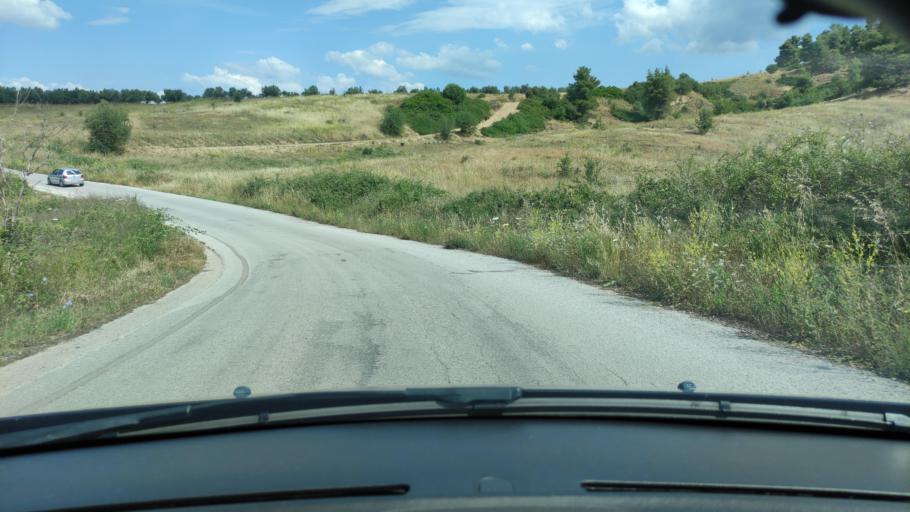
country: GR
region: Central Greece
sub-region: Nomos Evvoias
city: Afration
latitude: 38.5170
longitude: 23.7704
